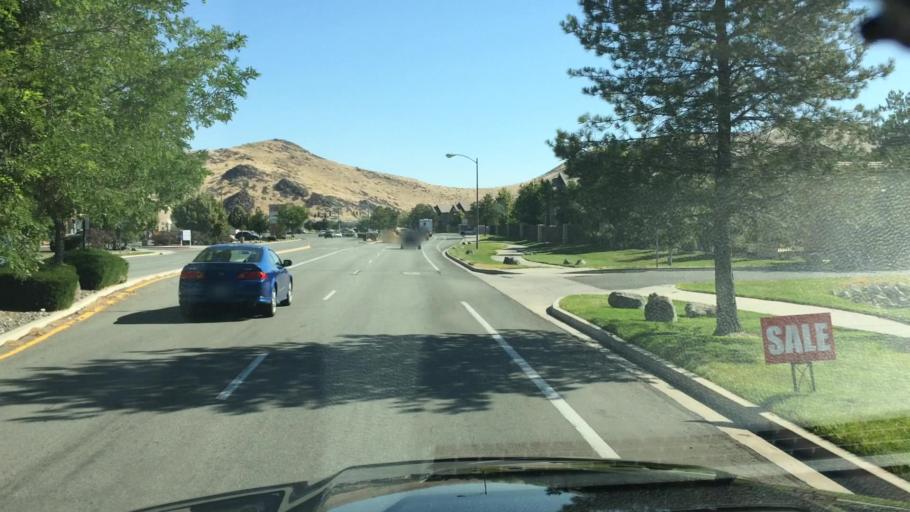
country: US
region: Nevada
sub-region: Washoe County
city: Sparks
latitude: 39.4491
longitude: -119.7591
